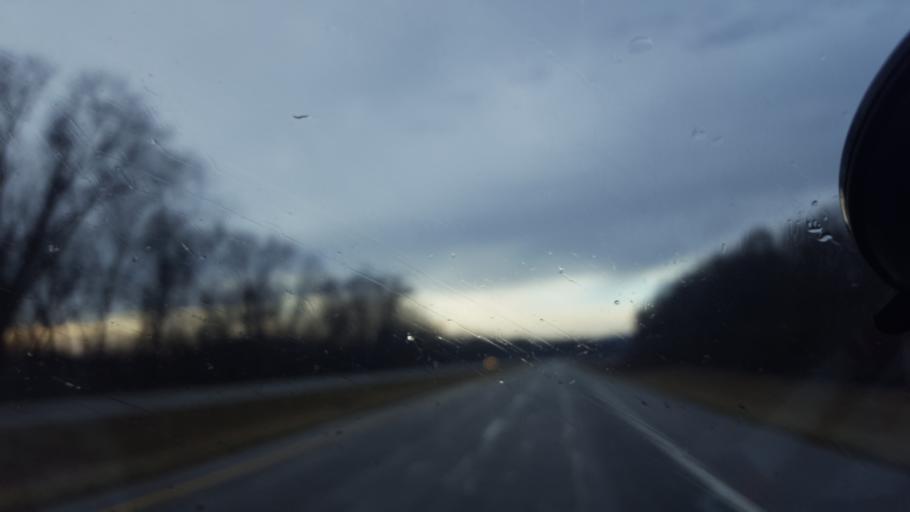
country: US
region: Ohio
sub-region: Coshocton County
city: West Lafayette
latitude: 40.2884
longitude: -81.7304
